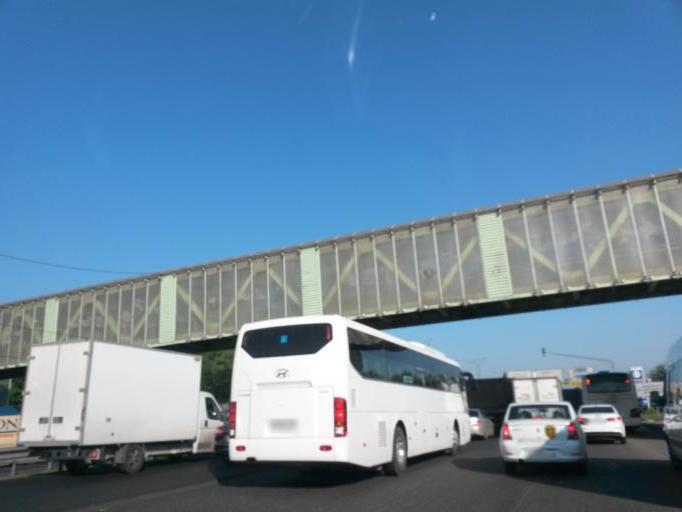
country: RU
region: Moskovskaya
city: Razvilka
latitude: 55.5883
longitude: 37.7346
